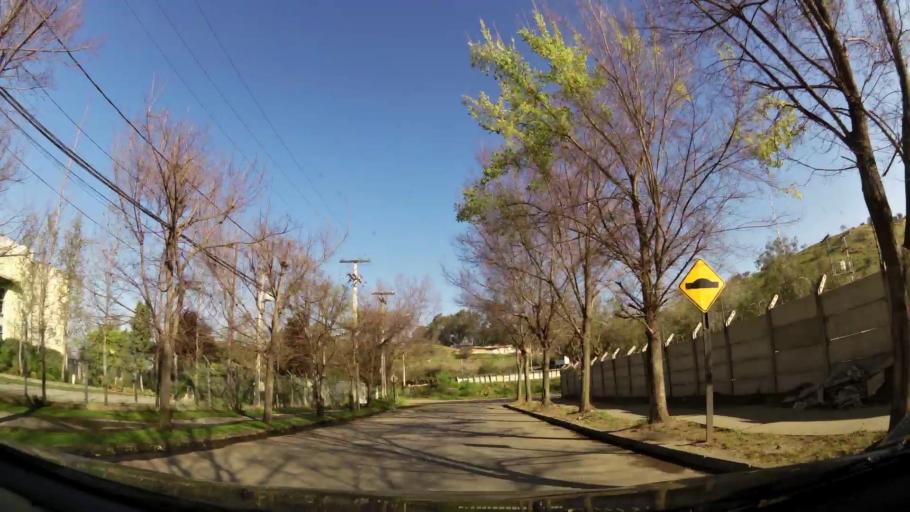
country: CL
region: Santiago Metropolitan
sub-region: Provincia de Santiago
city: Santiago
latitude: -33.3720
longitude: -70.6550
